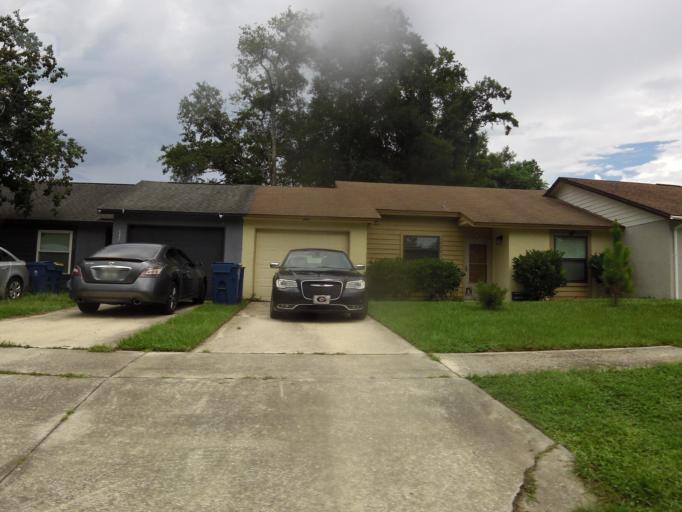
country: US
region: Florida
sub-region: Duval County
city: Jacksonville
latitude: 30.4307
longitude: -81.7013
